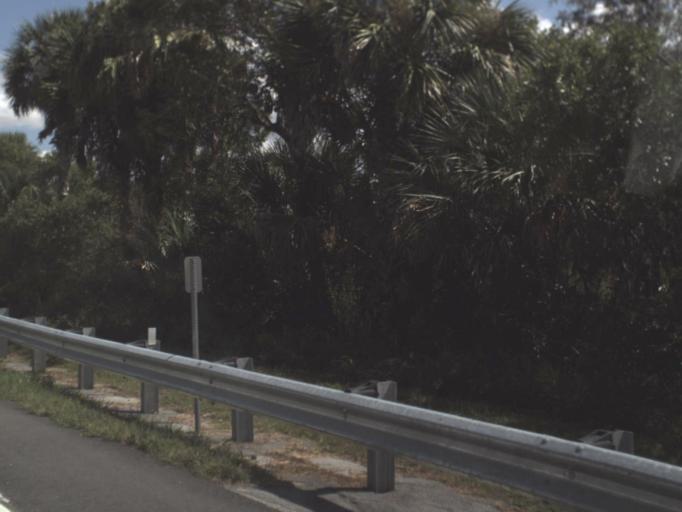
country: US
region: Florida
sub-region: Collier County
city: Lely Resort
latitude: 25.8647
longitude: -81.1101
